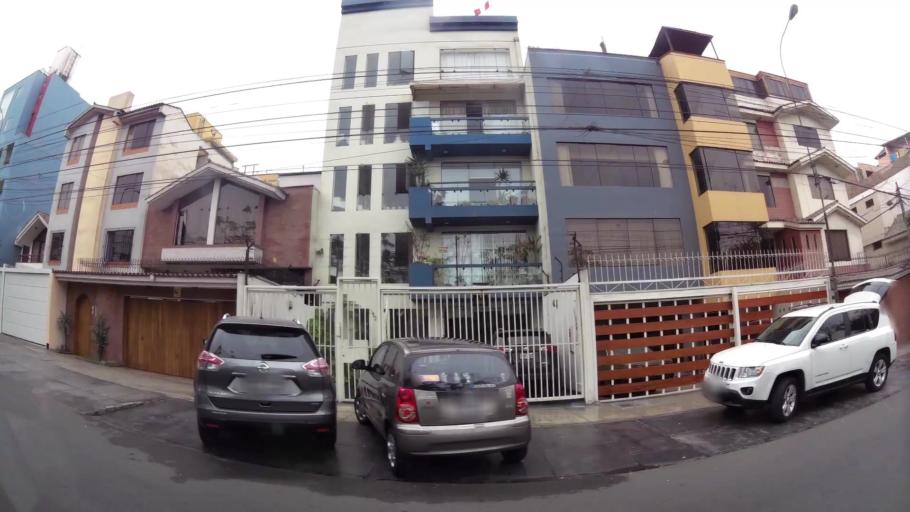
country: PE
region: Lima
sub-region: Lima
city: Surco
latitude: -12.1375
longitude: -76.9909
